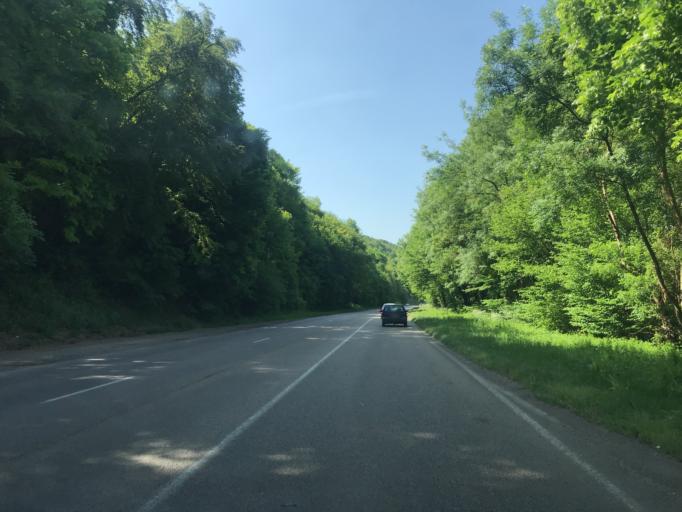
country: FR
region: Haute-Normandie
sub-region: Departement de la Seine-Maritime
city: Les Authieux-sur-le-Port-Saint-Ouen
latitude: 49.3463
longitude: 1.1266
